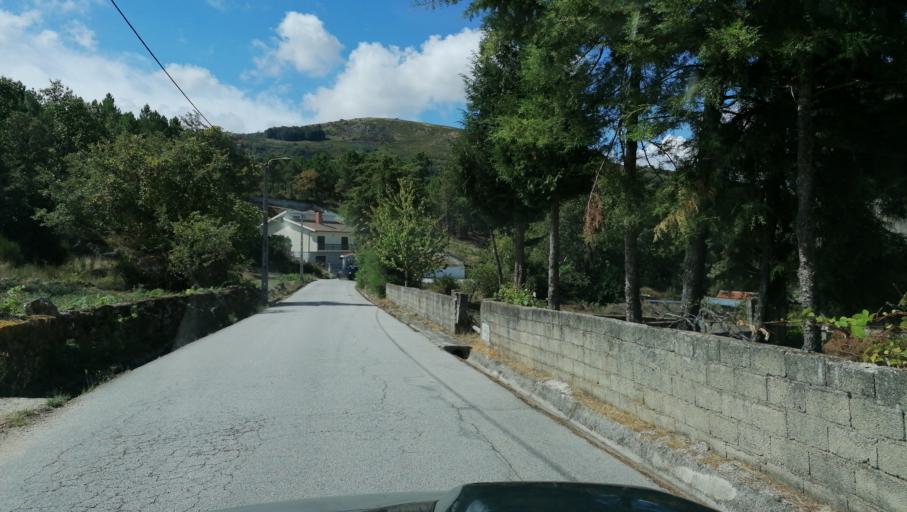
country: PT
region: Vila Real
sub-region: Vila Pouca de Aguiar
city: Vila Pouca de Aguiar
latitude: 41.5585
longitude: -7.6458
